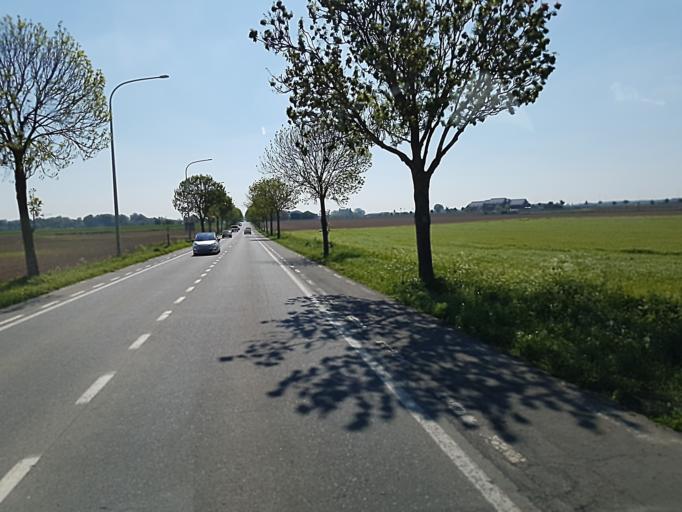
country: BE
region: Wallonia
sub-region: Province du Hainaut
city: Brugelette
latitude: 50.5934
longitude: 3.8332
